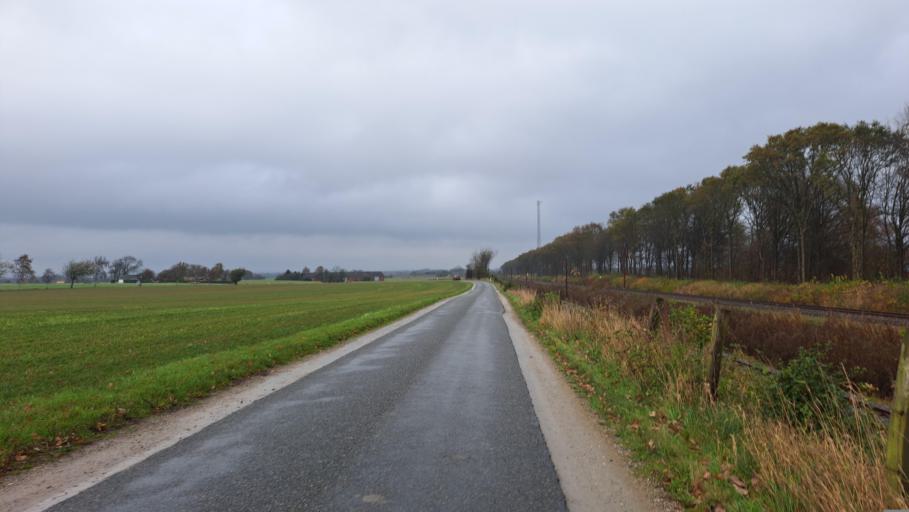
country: DK
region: Central Jutland
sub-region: Hedensted Kommune
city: Hedensted
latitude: 55.8261
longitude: 9.7296
